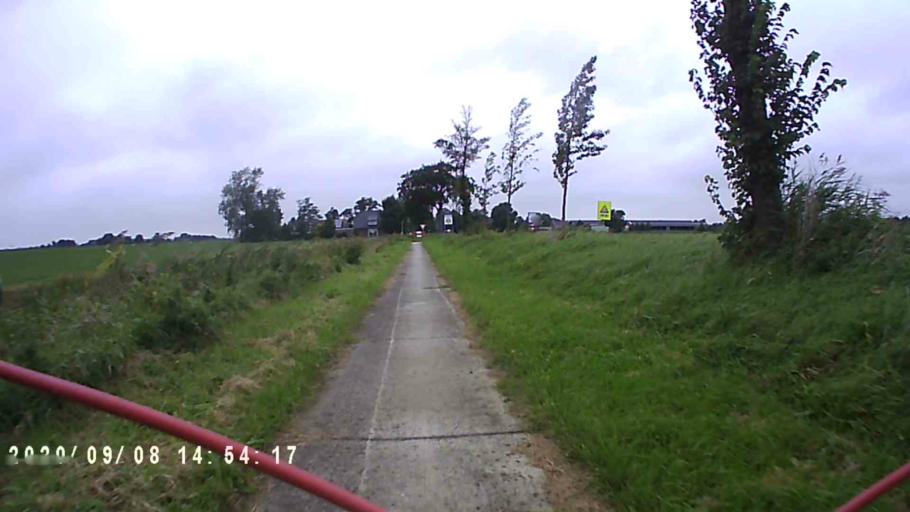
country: NL
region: Groningen
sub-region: Gemeente Slochteren
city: Slochteren
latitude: 53.2536
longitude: 6.7866
